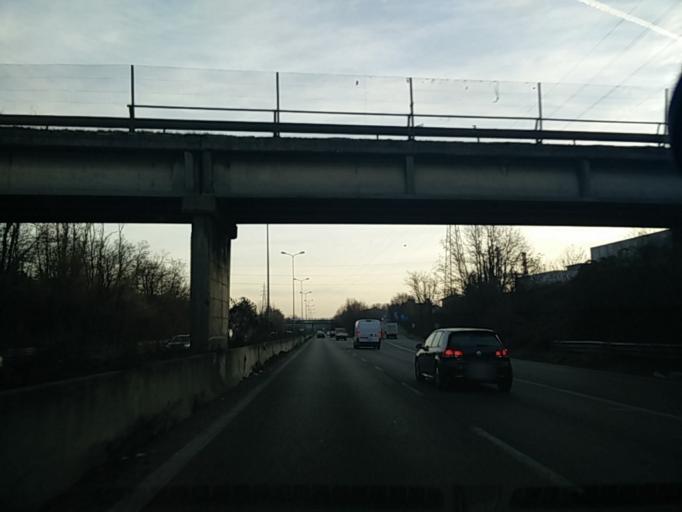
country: IT
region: Lombardy
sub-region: Provincia di Monza e Brianza
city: Bovisio-Masciago
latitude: 45.6165
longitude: 9.1651
